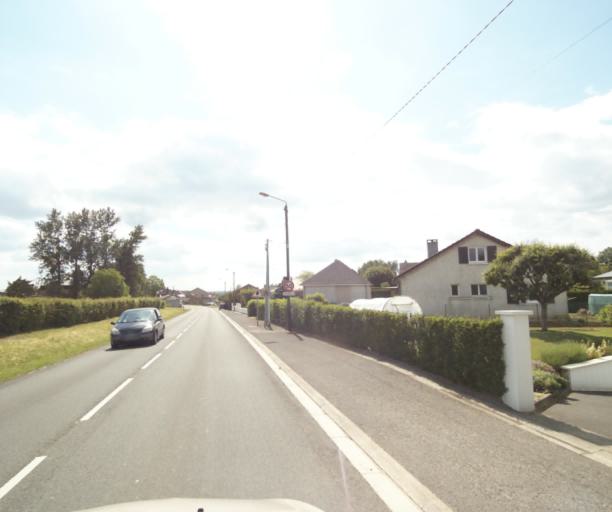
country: FR
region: Champagne-Ardenne
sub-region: Departement des Ardennes
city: Saint-Laurent
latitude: 49.7661
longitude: 4.7749
